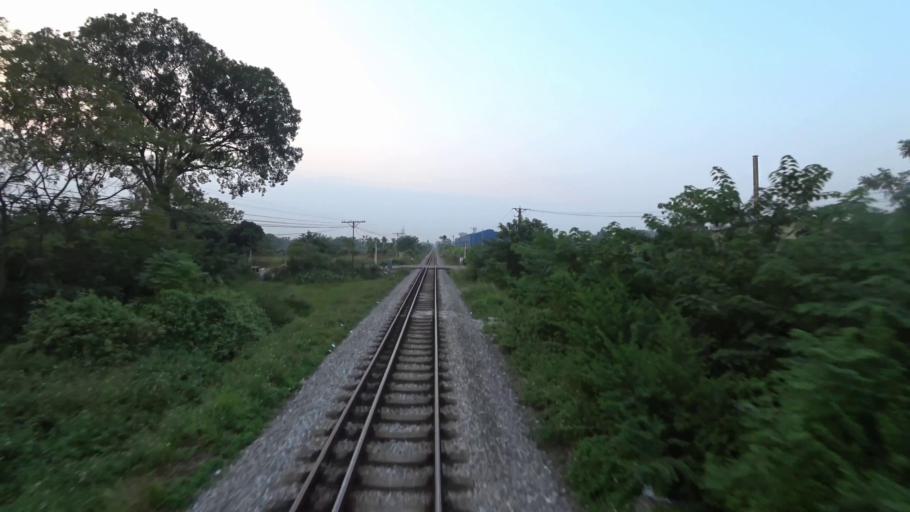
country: VN
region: Ha Noi
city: Dong Anh
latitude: 21.1452
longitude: 105.8611
